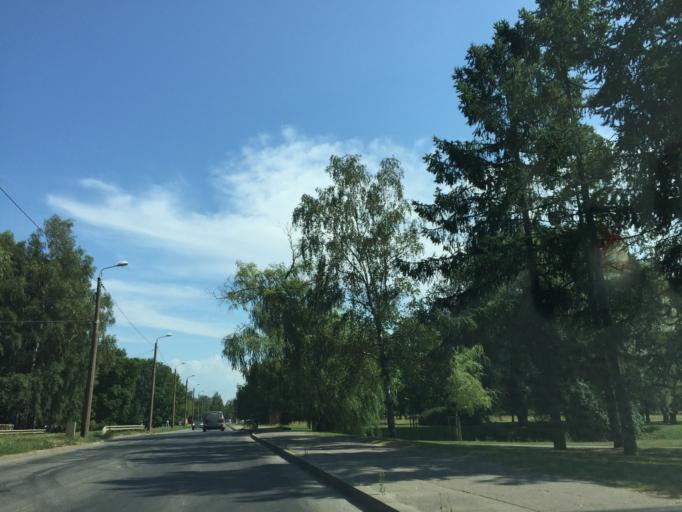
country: LV
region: Riga
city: Riga
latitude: 56.9410
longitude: 24.0859
